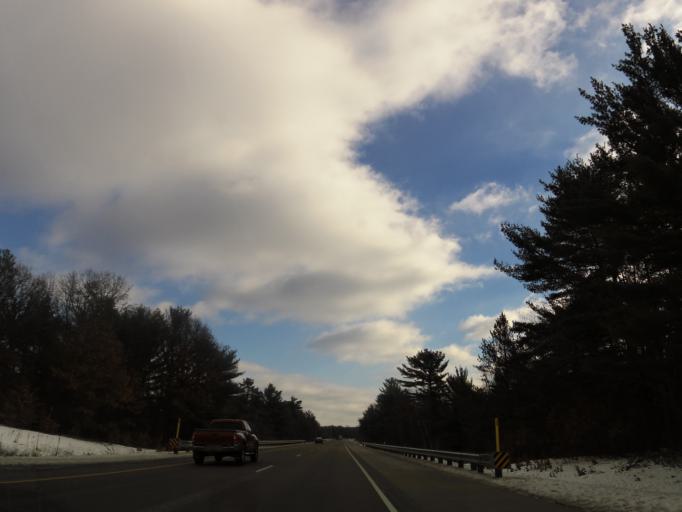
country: US
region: Wisconsin
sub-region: Jackson County
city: Black River Falls
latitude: 44.2431
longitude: -90.7323
